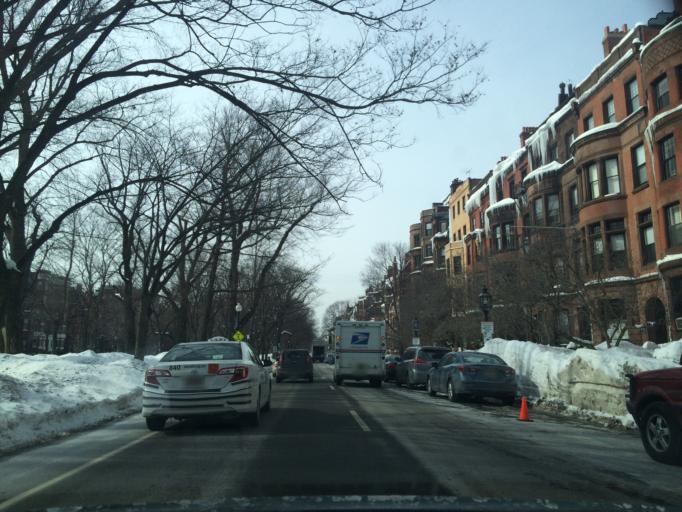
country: US
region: Massachusetts
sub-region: Suffolk County
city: Boston
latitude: 42.3512
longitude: -71.0816
